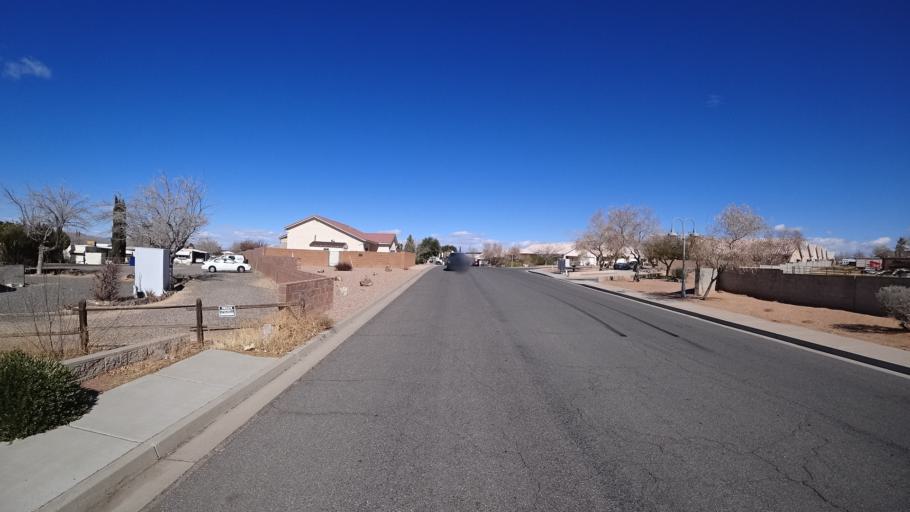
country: US
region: Arizona
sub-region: Mohave County
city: Kingman
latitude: 35.1886
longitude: -114.0098
